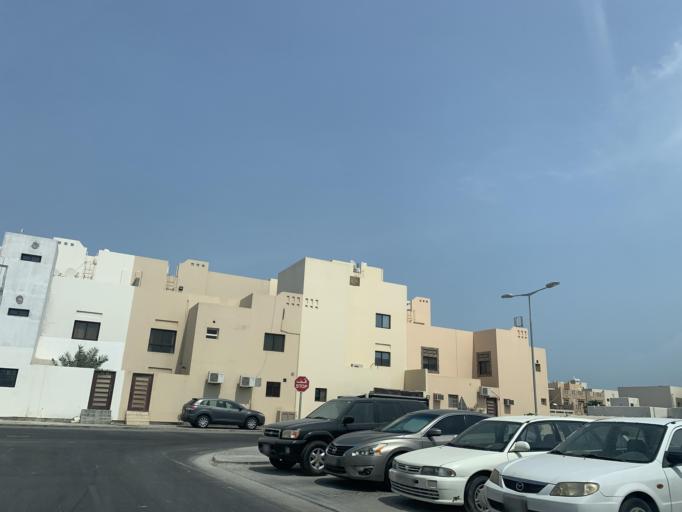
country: BH
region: Muharraq
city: Al Hadd
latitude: 26.2680
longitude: 50.6588
